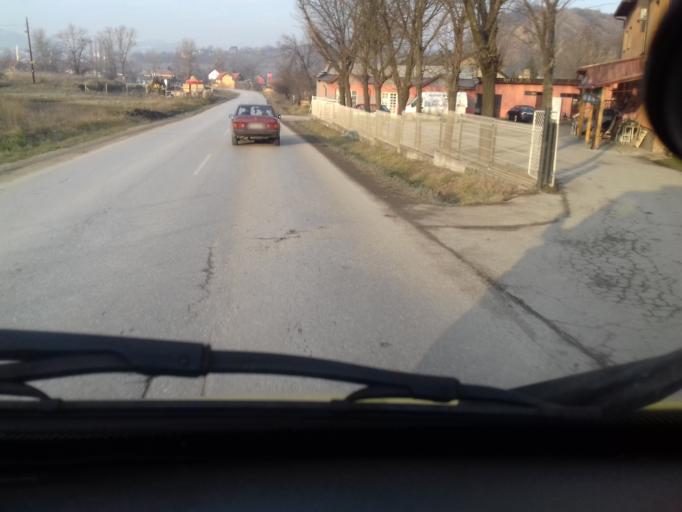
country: BA
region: Federation of Bosnia and Herzegovina
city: Kakanj
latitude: 44.1081
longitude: 18.1189
